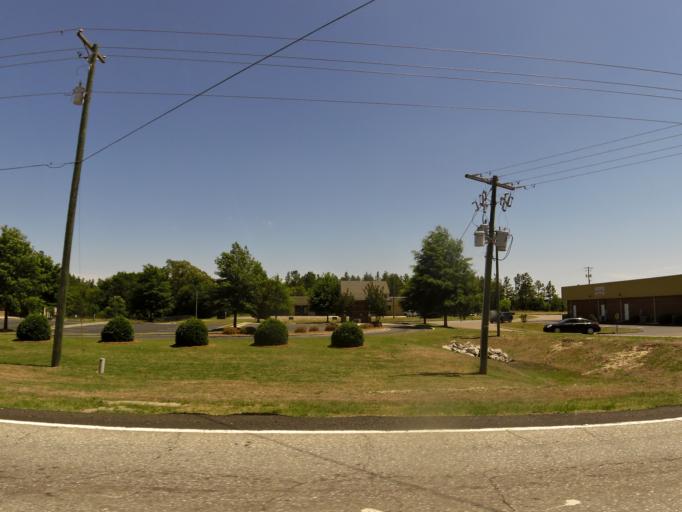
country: US
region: South Carolina
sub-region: Aiken County
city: Langley
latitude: 33.5276
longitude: -81.8464
